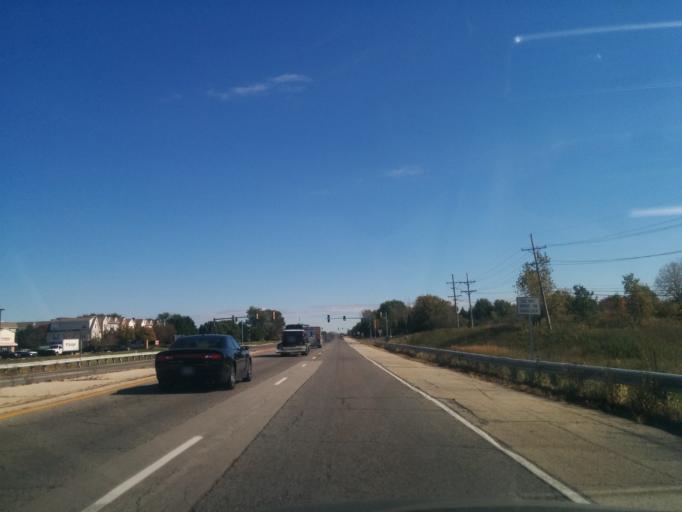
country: US
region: Illinois
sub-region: DuPage County
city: Lisle
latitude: 41.8291
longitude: -88.0955
